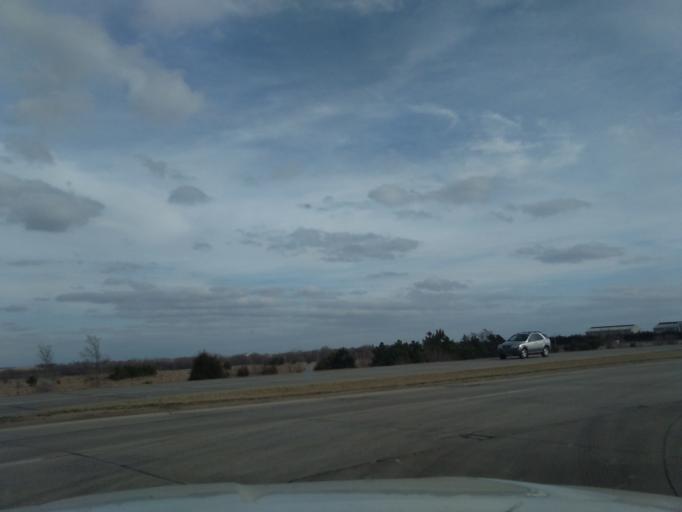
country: US
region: Nebraska
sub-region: Gage County
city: Beatrice
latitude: 40.3209
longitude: -96.7472
